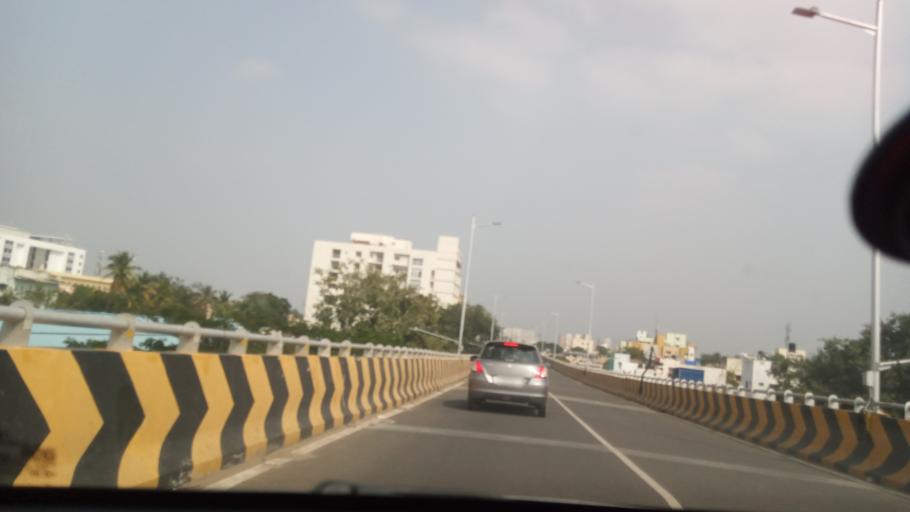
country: IN
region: Tamil Nadu
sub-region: Coimbatore
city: Coimbatore
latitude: 11.0211
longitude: 76.9753
